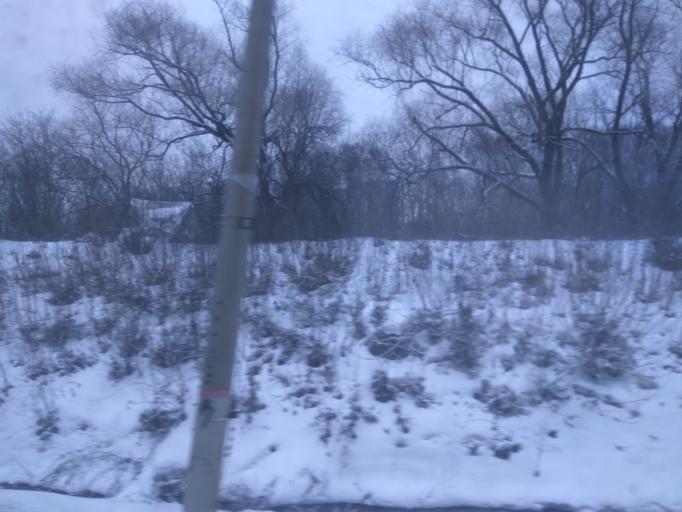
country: RU
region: Moskovskaya
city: Shcherbinka
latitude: 55.4673
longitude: 37.5559
